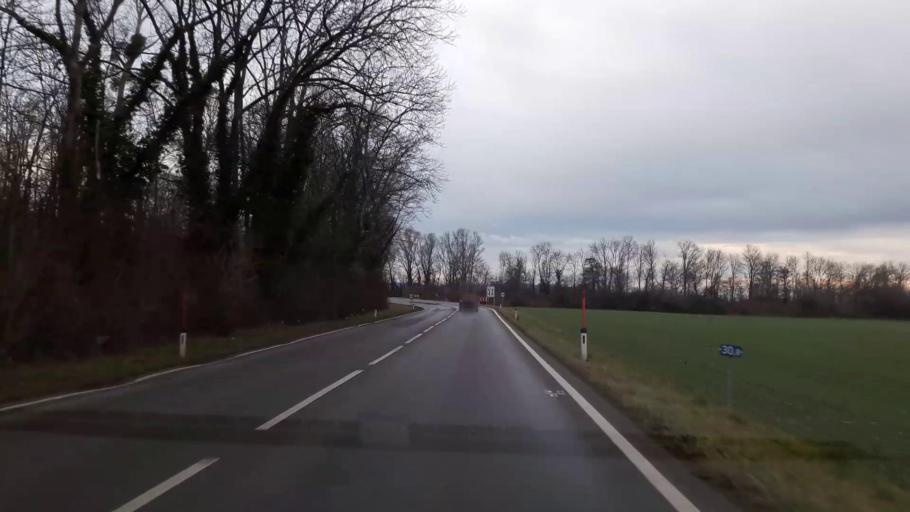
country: AT
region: Lower Austria
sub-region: Politischer Bezirk Baden
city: Ebreichsdorf
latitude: 47.9596
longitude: 16.3920
